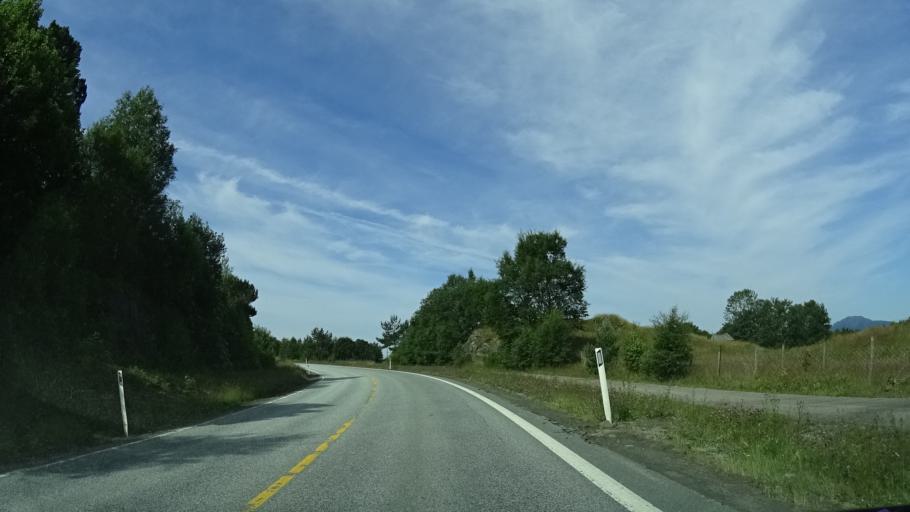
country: NO
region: Hordaland
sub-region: Bomlo
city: Mosterhamn
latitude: 59.6737
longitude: 5.4636
